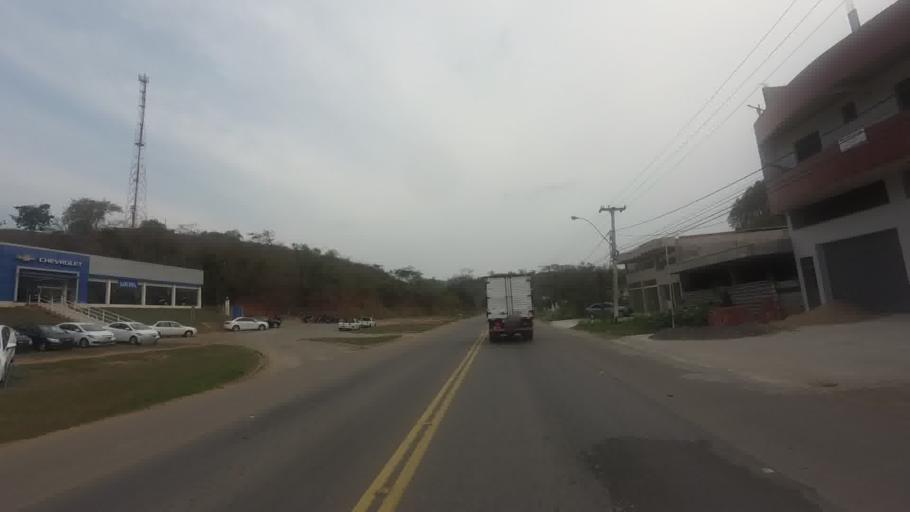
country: BR
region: Rio de Janeiro
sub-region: Santo Antonio De Padua
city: Santo Antonio de Padua
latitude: -21.5548
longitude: -42.1792
